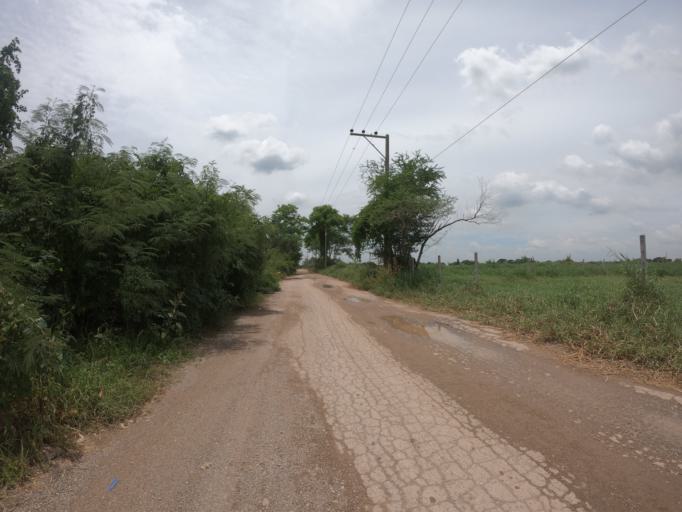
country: TH
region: Pathum Thani
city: Ban Lam Luk Ka
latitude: 13.9861
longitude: 100.8492
